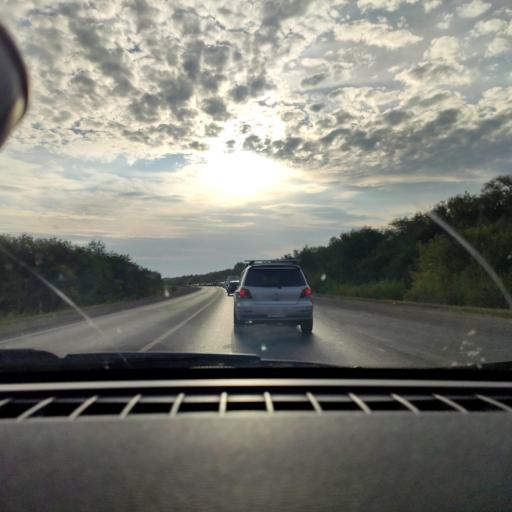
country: RU
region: Samara
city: Samara
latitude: 53.0811
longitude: 50.1259
